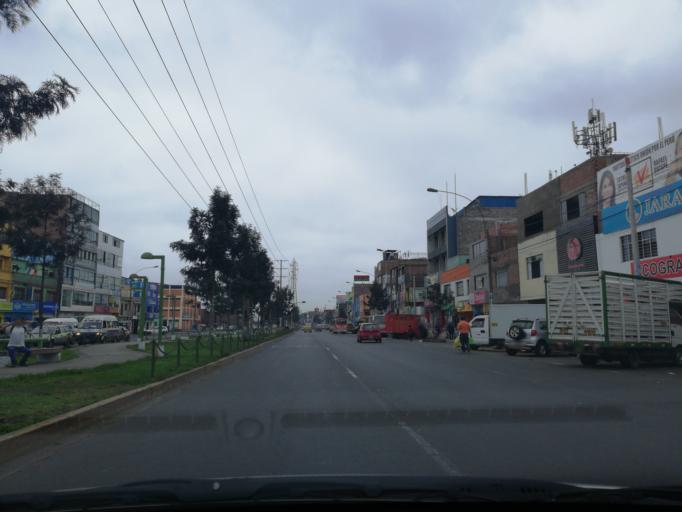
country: PE
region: Lima
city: Lima
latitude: -12.0321
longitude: -77.0651
